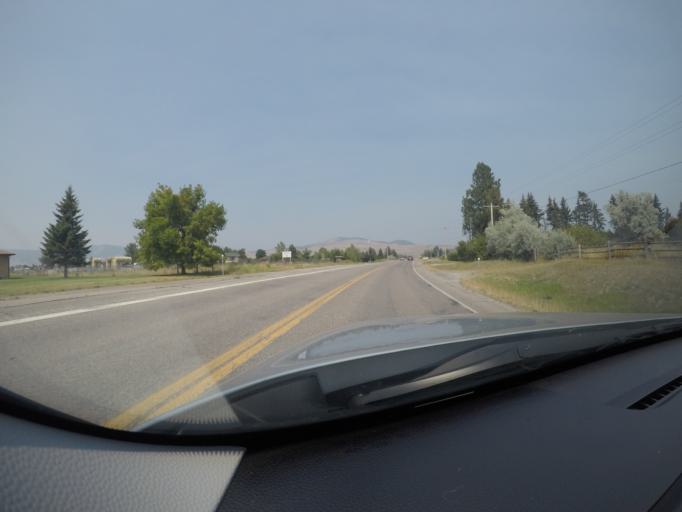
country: US
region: Montana
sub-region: Lake County
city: Polson
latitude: 47.7151
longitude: -114.1885
